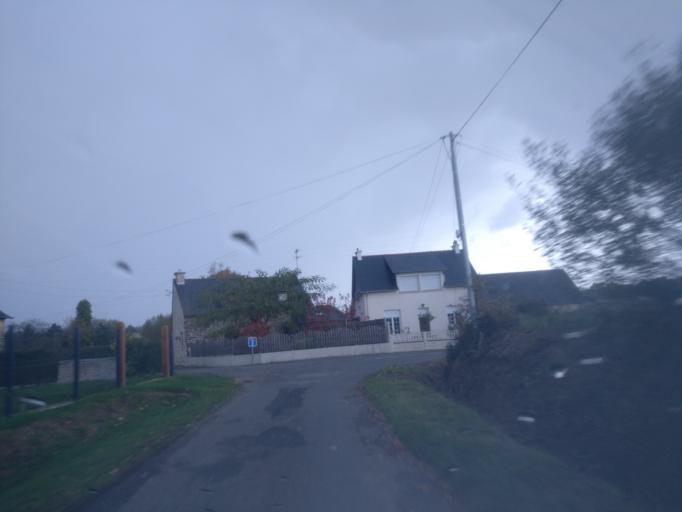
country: FR
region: Brittany
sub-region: Departement d'Ille-et-Vilaine
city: Bruz
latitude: 48.0077
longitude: -1.7810
